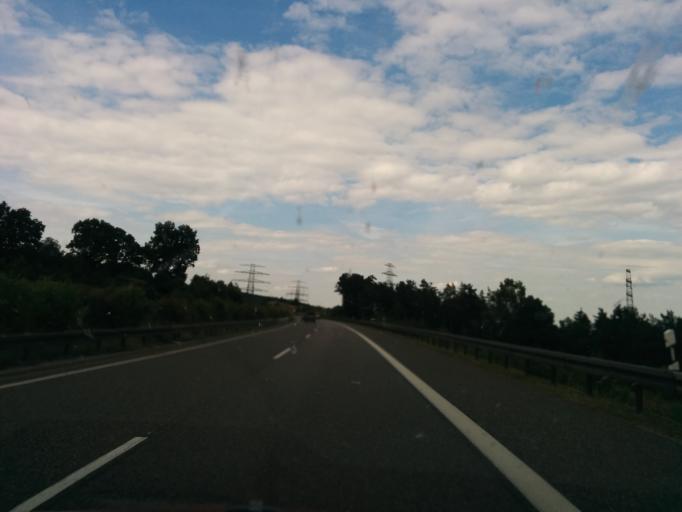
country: DE
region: Thuringia
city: Behringen
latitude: 50.7468
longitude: 10.9970
